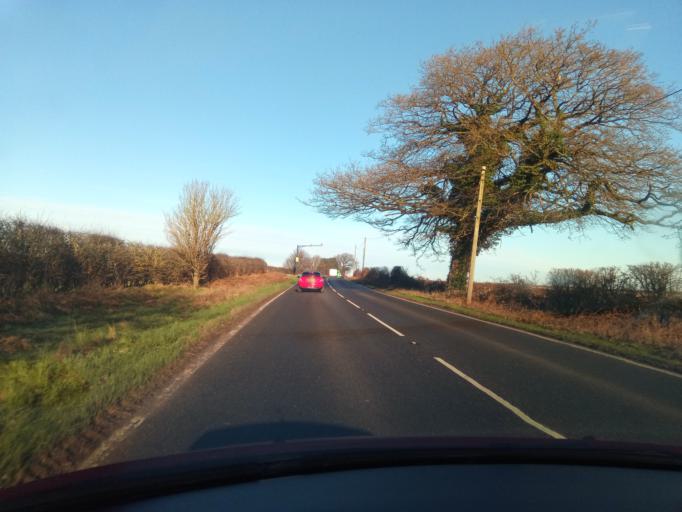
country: GB
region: England
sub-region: Nottinghamshire
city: Farnsfield
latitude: 53.0850
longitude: -1.0698
